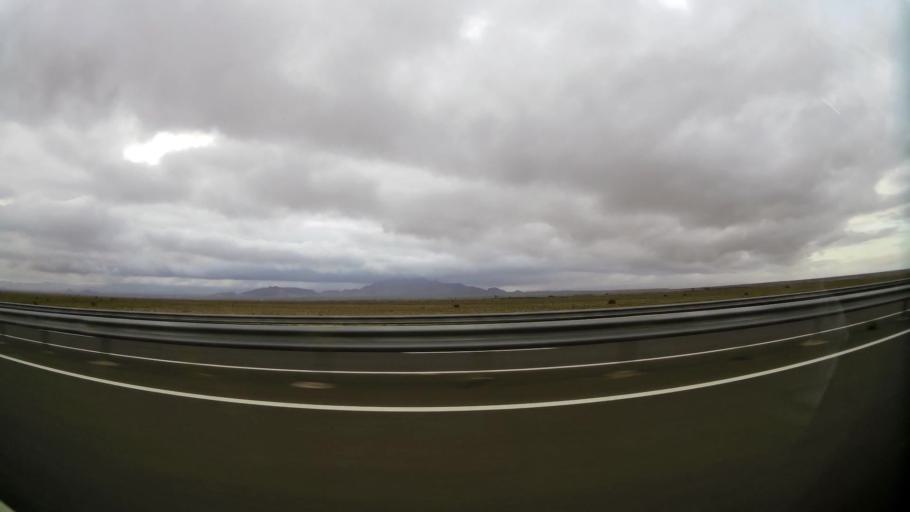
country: MA
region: Taza-Al Hoceima-Taounate
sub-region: Taza
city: Guercif
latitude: 34.3776
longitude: -3.2504
